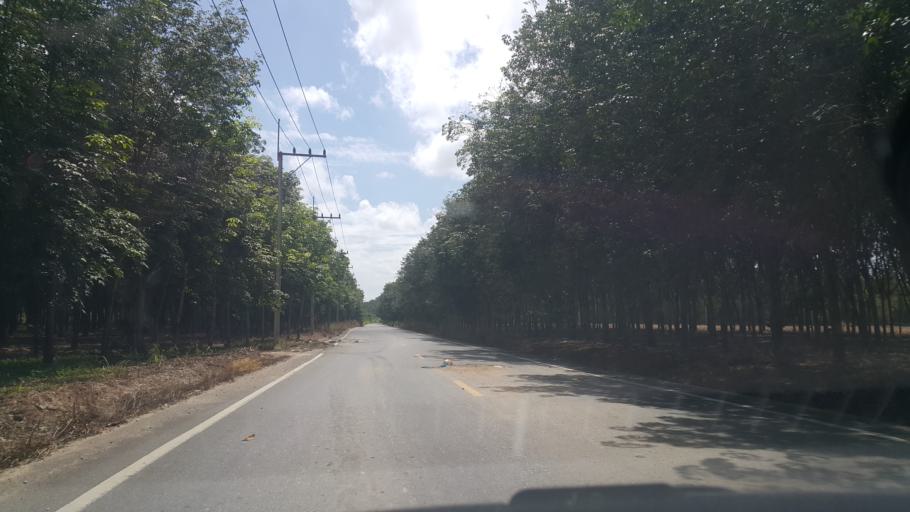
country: TH
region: Rayong
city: Ban Chang
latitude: 12.8089
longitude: 101.0012
